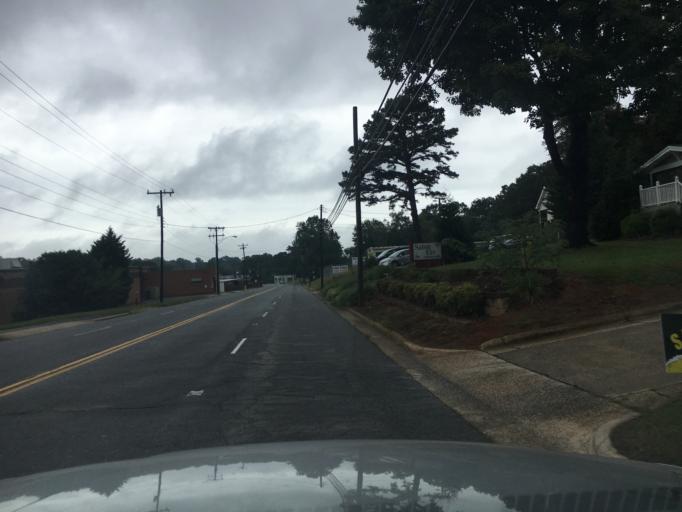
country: US
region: North Carolina
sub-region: Catawba County
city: Hickory
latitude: 35.7411
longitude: -81.3592
